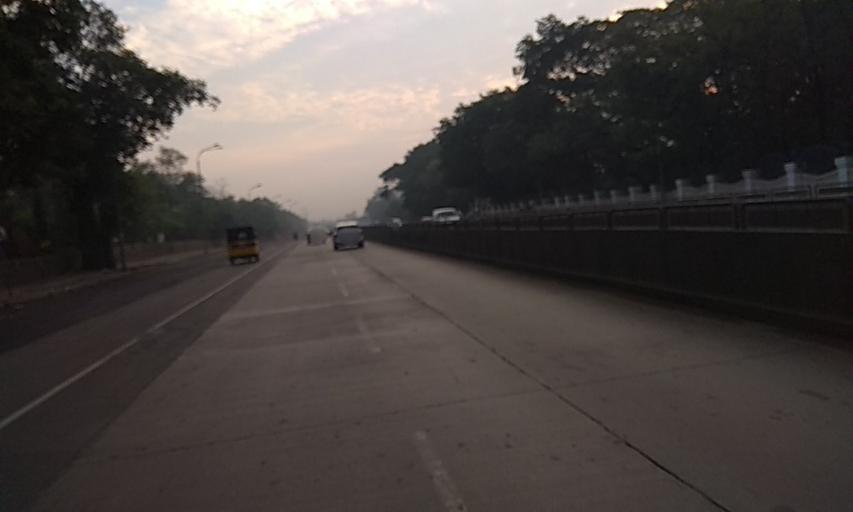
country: IN
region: Maharashtra
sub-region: Pune Division
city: Khadki
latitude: 18.5537
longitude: 73.9010
